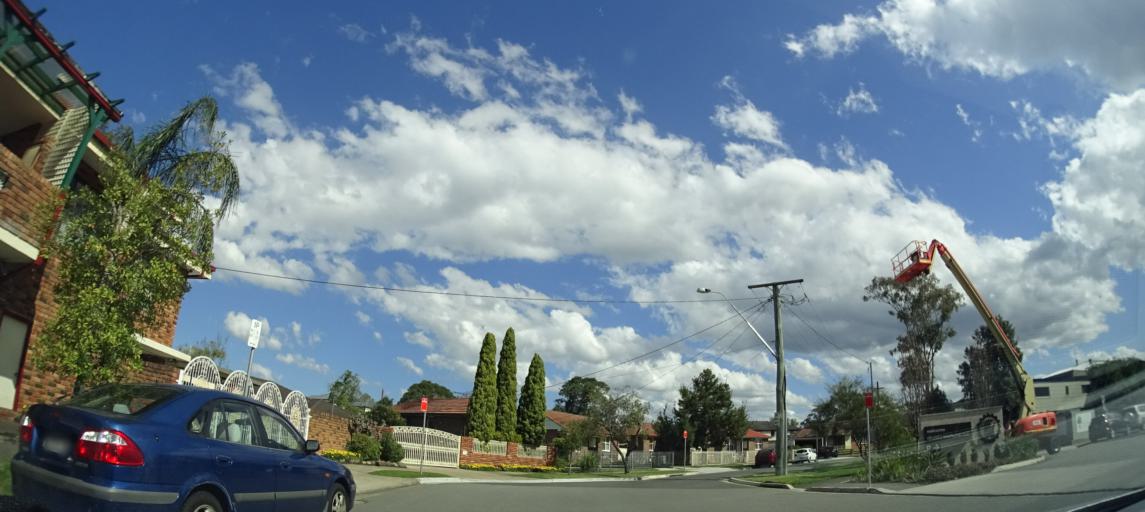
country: AU
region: New South Wales
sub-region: Bankstown
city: Revesby
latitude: -33.9538
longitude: 151.0144
